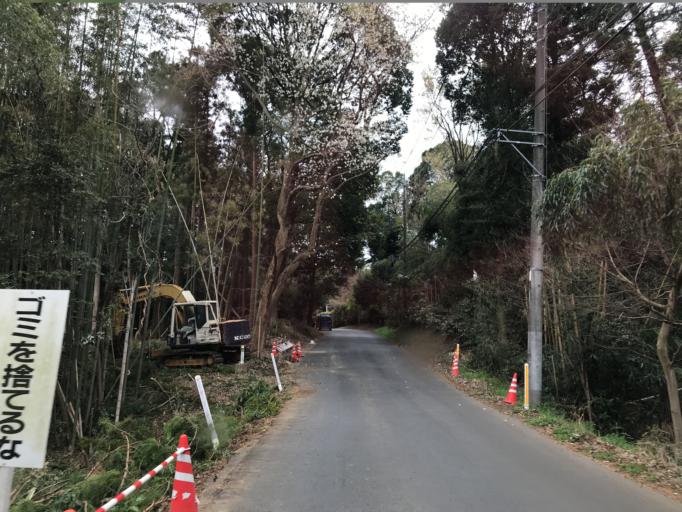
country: JP
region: Ibaraki
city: Moriya
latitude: 35.9584
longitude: 140.0058
